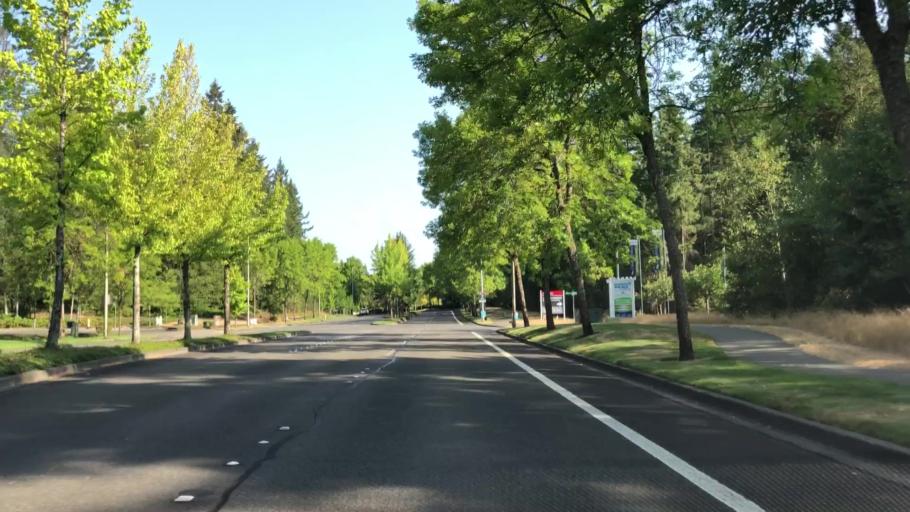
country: US
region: Washington
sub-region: Thurston County
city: Tanglewilde-Thompson Place
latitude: 47.0868
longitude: -122.7559
